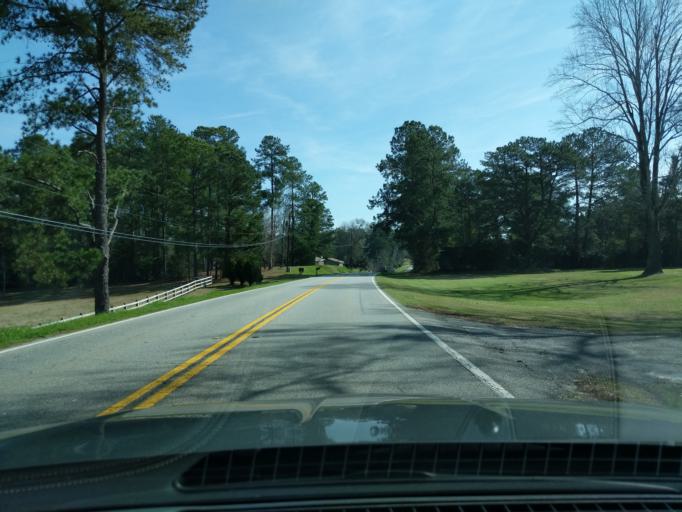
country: US
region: Georgia
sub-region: Columbia County
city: Evans
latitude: 33.5330
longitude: -82.1407
